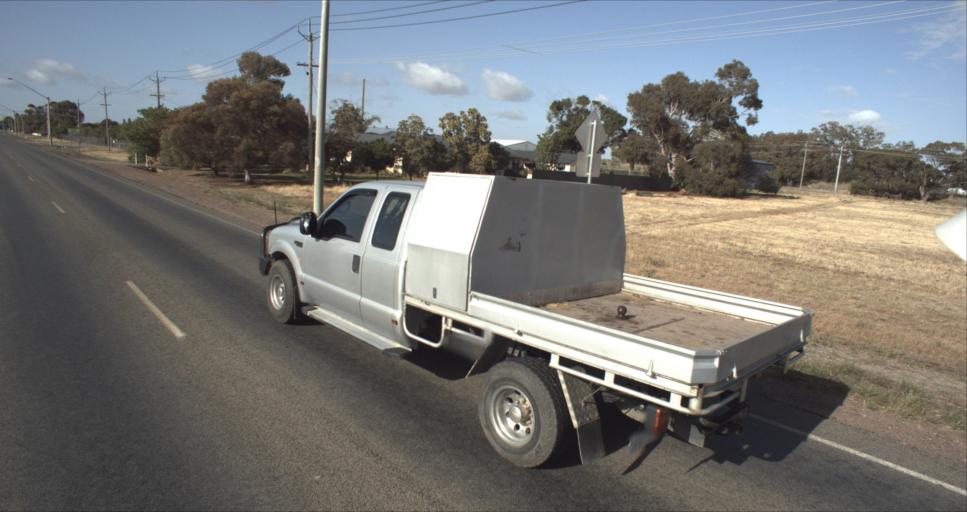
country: AU
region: New South Wales
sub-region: Leeton
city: Leeton
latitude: -34.5626
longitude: 146.3927
